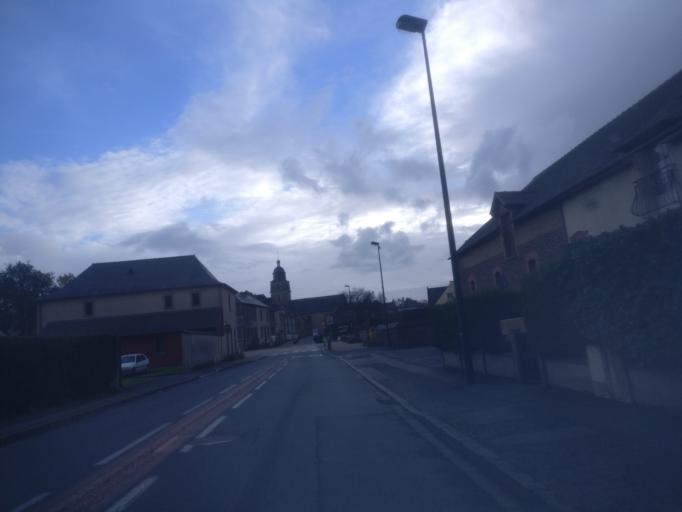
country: FR
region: Brittany
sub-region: Departement d'Ille-et-Vilaine
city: Breal-sous-Montfort
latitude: 48.0504
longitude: -1.8684
